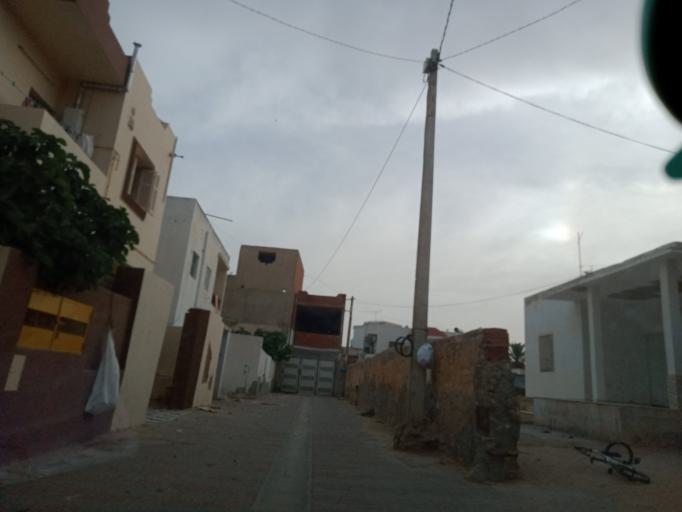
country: TN
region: Safaqis
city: Al Qarmadah
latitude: 34.8041
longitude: 10.7563
